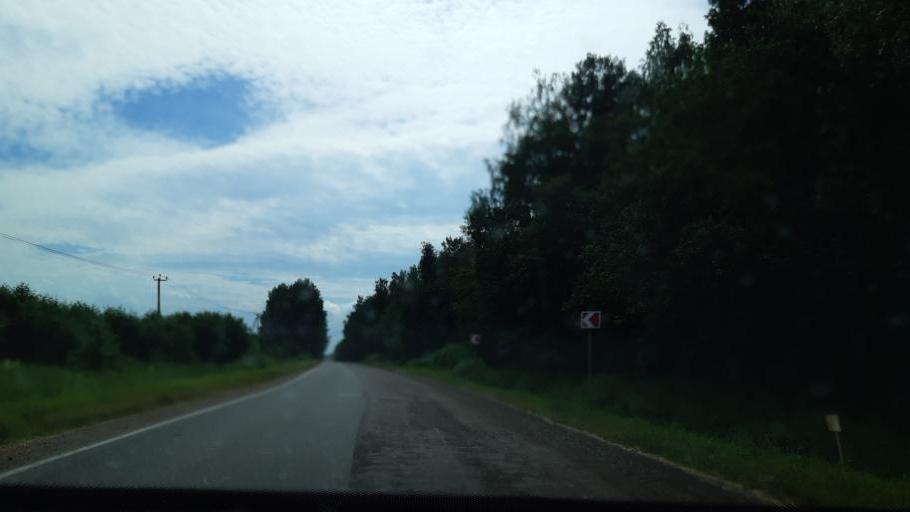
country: RU
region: Moskovskaya
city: Vereya
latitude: 55.2508
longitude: 36.0569
